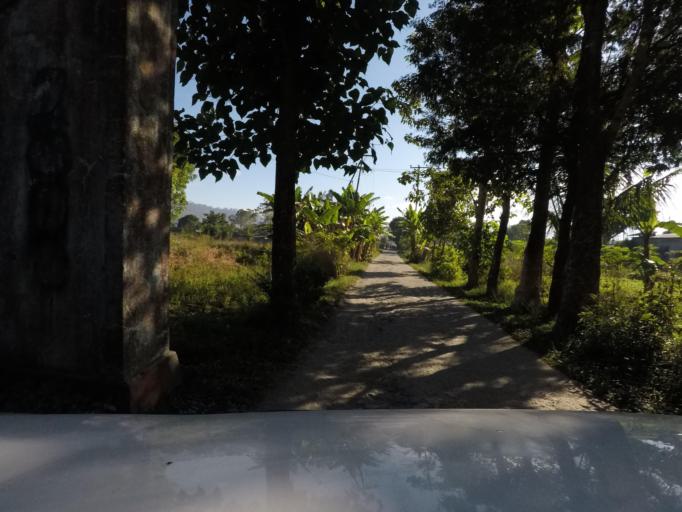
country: TL
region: Ermera
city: Gleno
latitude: -8.7276
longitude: 125.4303
